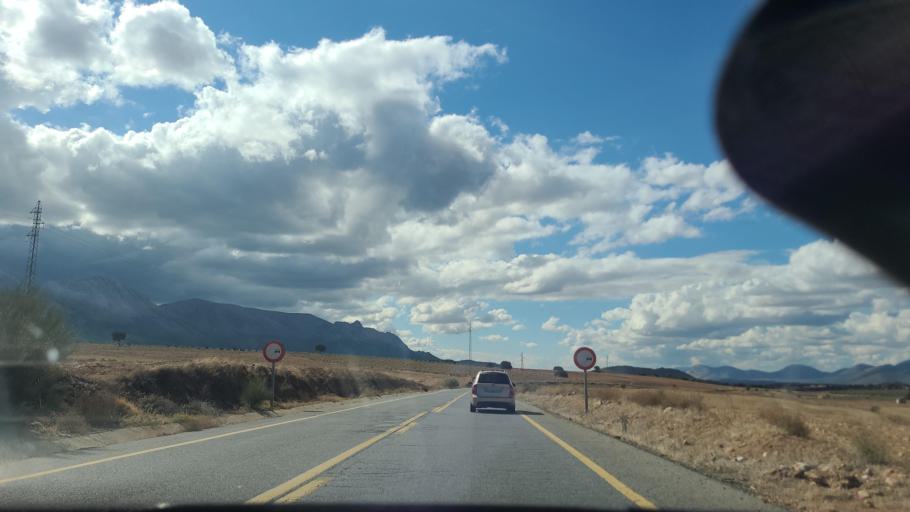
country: ES
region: Andalusia
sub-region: Provincia de Granada
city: Pinar
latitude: 37.3985
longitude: -3.4171
